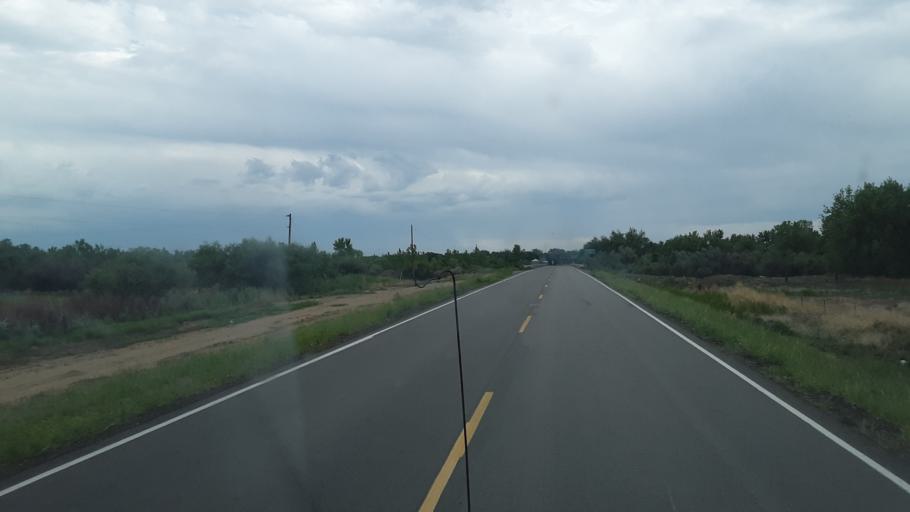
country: US
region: Colorado
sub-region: Otero County
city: Fowler
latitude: 38.1432
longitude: -104.0228
